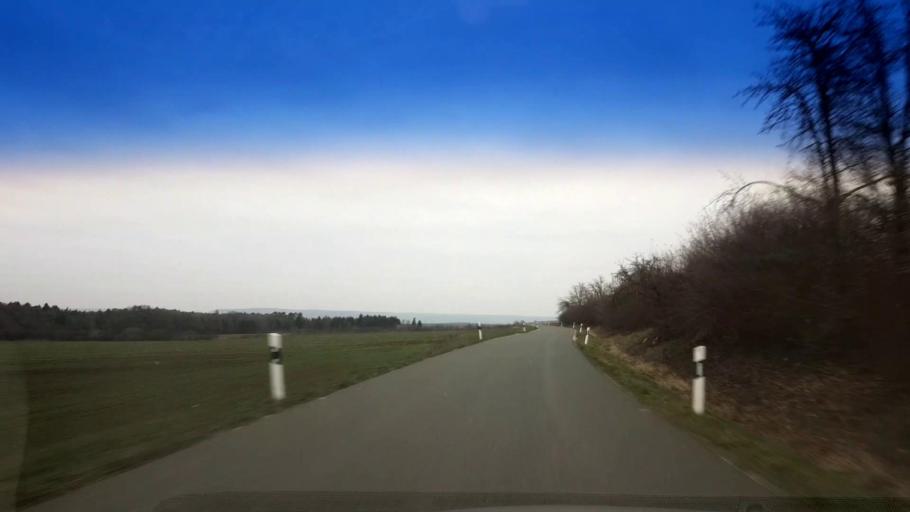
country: DE
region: Bavaria
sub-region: Upper Franconia
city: Hallerndorf
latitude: 49.7687
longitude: 10.9331
